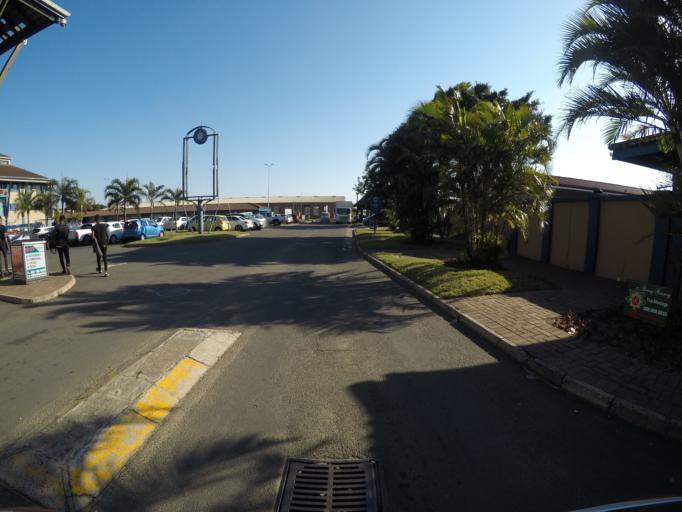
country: ZA
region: KwaZulu-Natal
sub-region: uThungulu District Municipality
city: Richards Bay
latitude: -28.7931
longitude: 32.0784
